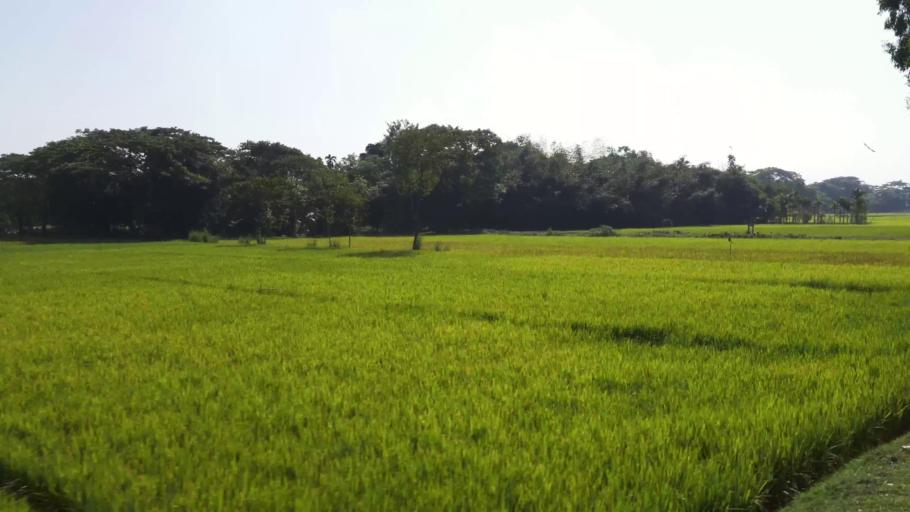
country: BD
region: Dhaka
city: Gafargaon
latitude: 24.5057
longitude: 90.5175
